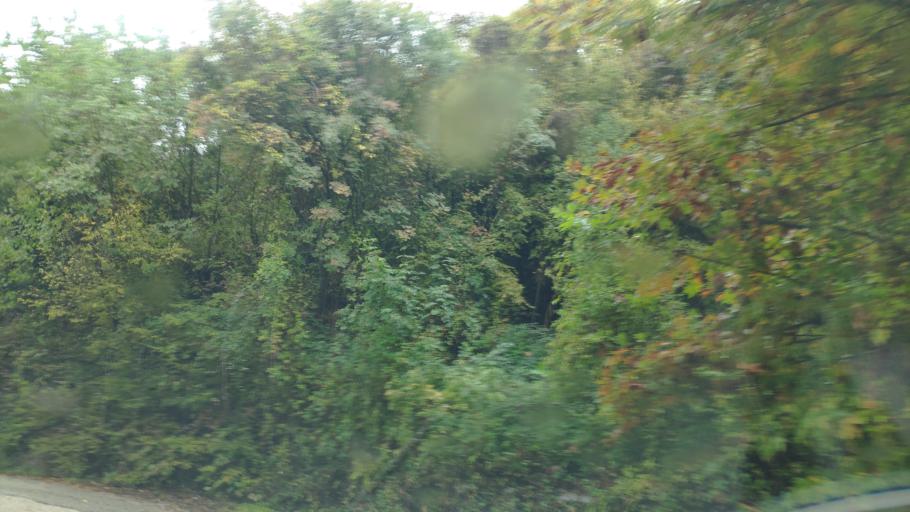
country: GR
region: Epirus
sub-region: Nomos Thesprotias
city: Paramythia
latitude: 39.4631
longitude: 20.6709
